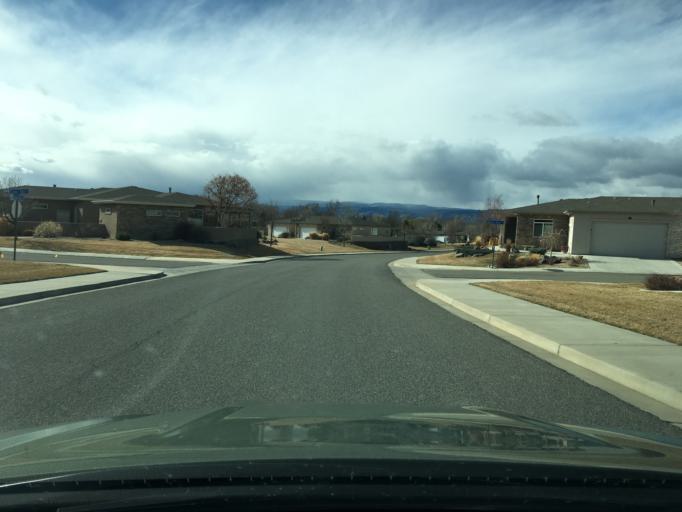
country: US
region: Colorado
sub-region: Mesa County
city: Grand Junction
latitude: 39.1291
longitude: -108.5569
